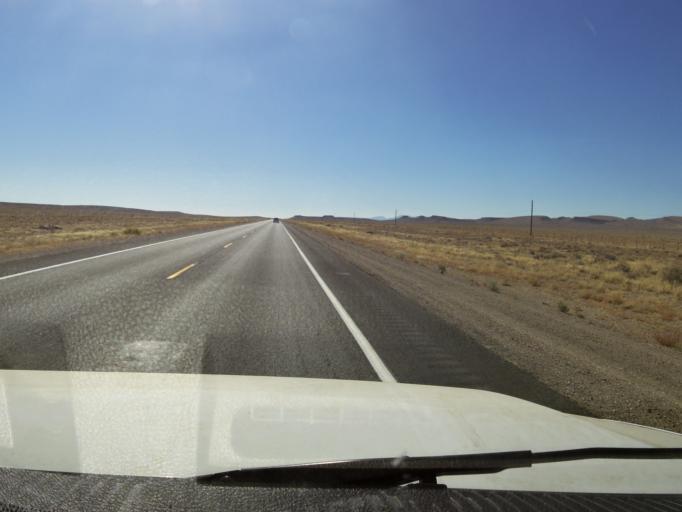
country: US
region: Nevada
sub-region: Esmeralda County
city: Goldfield
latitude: 37.4274
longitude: -117.1594
